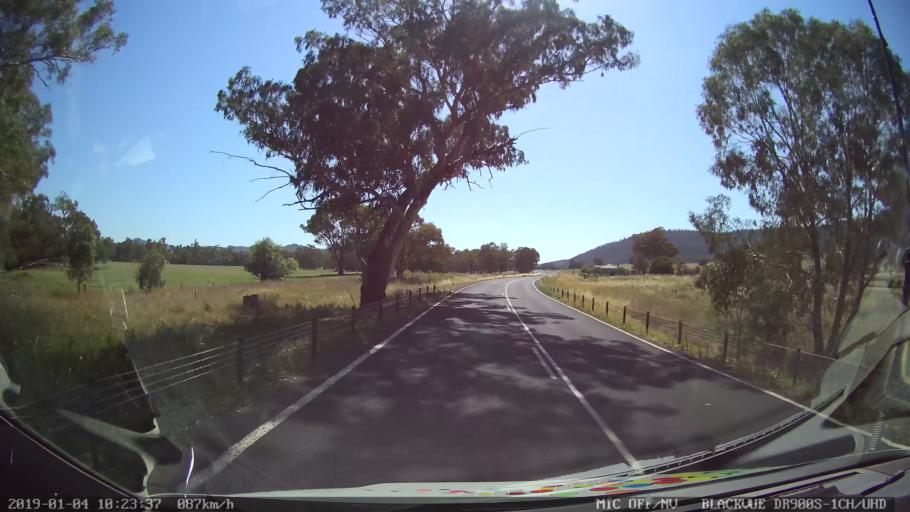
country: AU
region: New South Wales
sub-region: Cabonne
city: Canowindra
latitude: -33.3705
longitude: 148.5420
